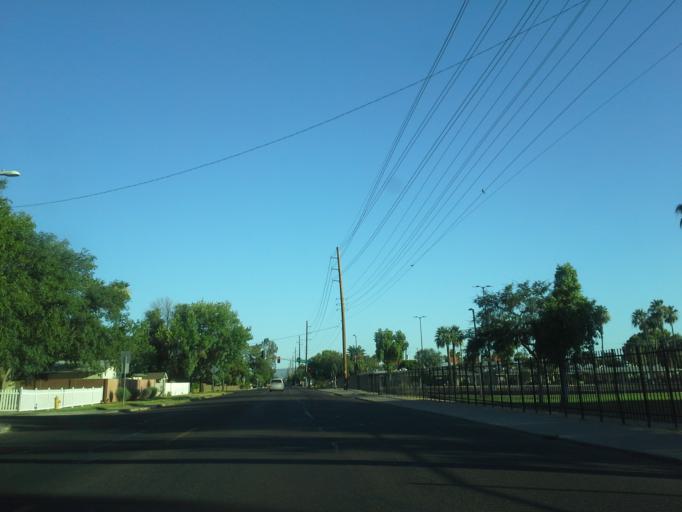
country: US
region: Arizona
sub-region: Maricopa County
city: Phoenix
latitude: 33.5036
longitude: -112.0217
